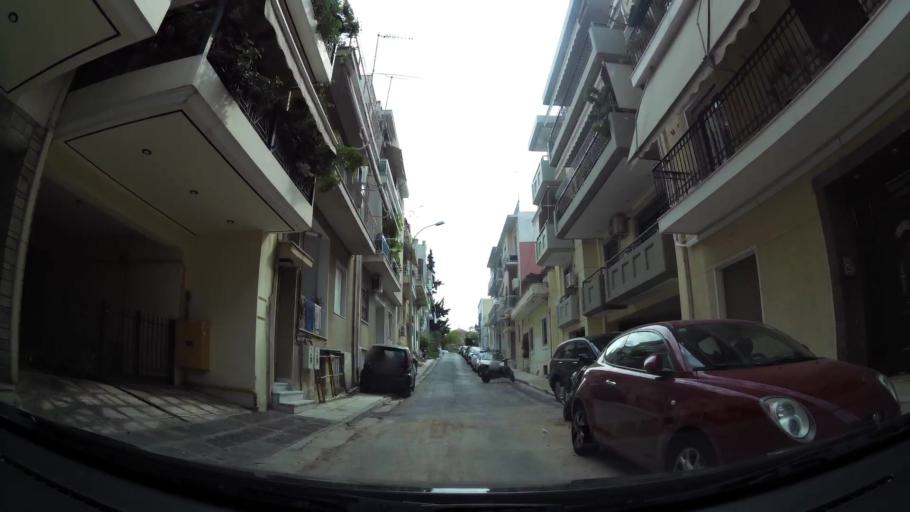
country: GR
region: Attica
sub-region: Nomarchia Athinas
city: Athens
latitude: 37.9655
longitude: 23.7153
